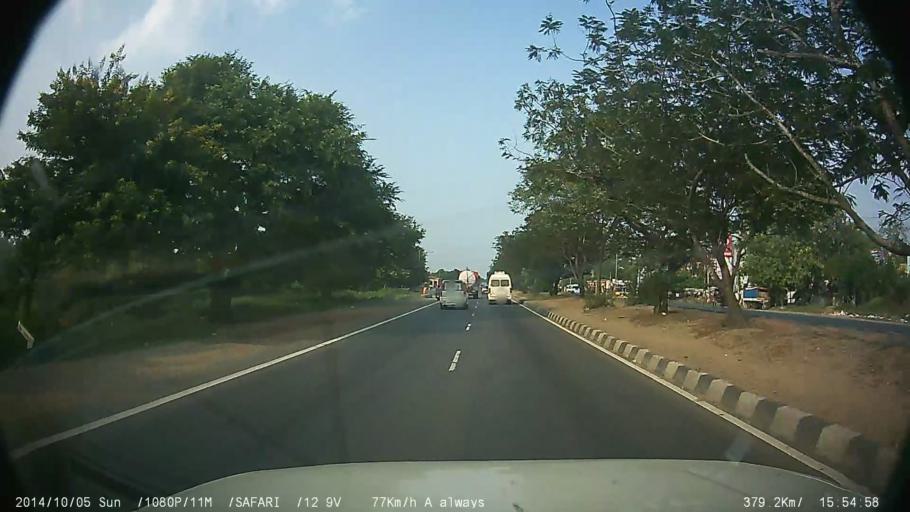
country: IN
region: Tamil Nadu
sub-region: Kancheepuram
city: Singapperumalkovil
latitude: 12.7981
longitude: 80.0221
